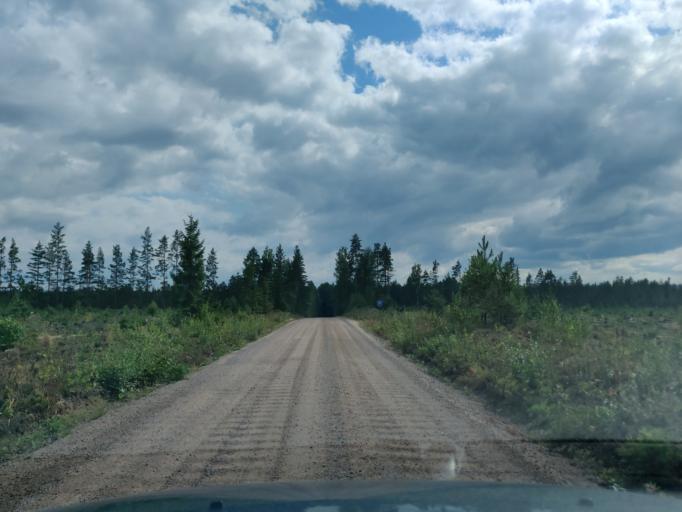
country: SE
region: Vaermland
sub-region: Hagfors Kommun
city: Hagfors
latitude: 59.9765
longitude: 13.5485
